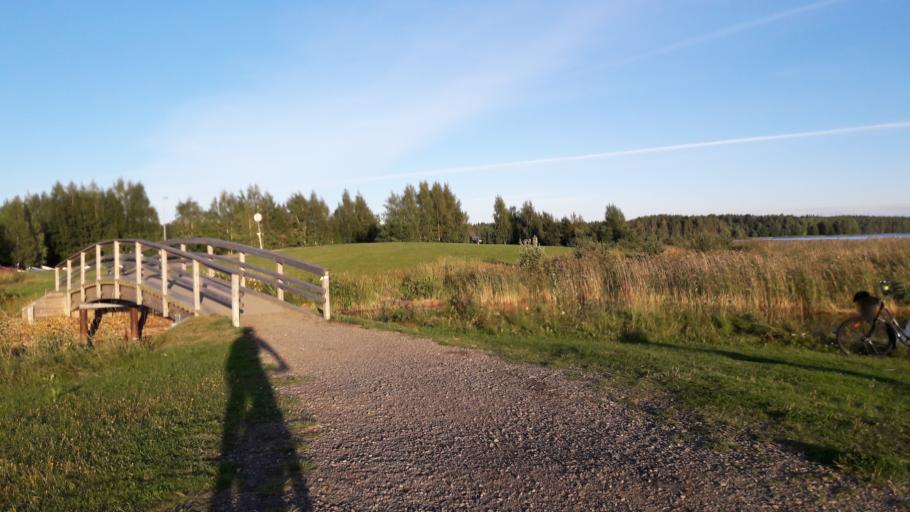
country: FI
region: North Karelia
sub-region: Joensuu
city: Joensuu
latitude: 62.6125
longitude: 29.7062
